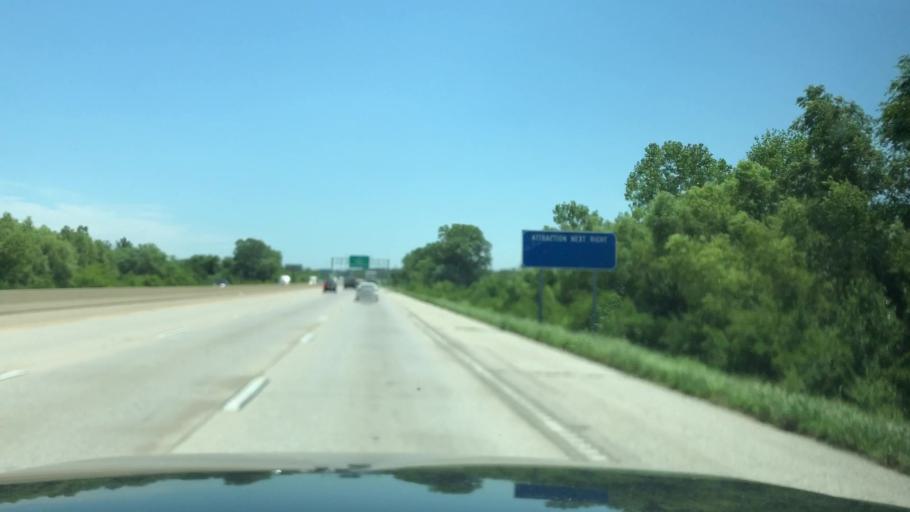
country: US
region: Missouri
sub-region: Saint Louis County
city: Bridgeton
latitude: 38.7908
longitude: -90.4366
